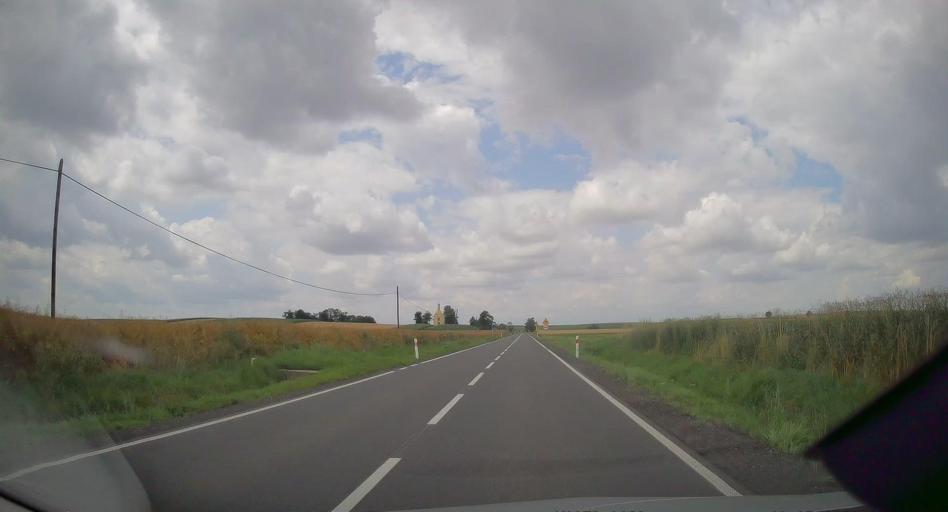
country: PL
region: Opole Voivodeship
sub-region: Powiat prudnicki
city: Glogowek
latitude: 50.3537
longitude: 17.8328
